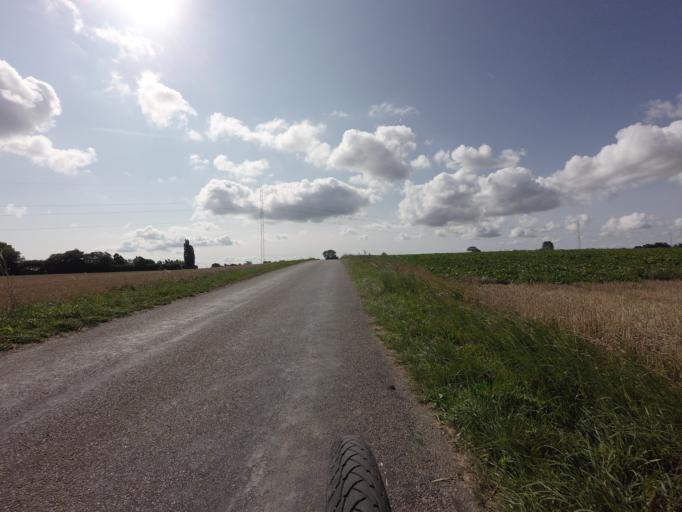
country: DK
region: Zealand
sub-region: Vordingborg Kommune
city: Stege
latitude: 54.9708
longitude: 12.3391
